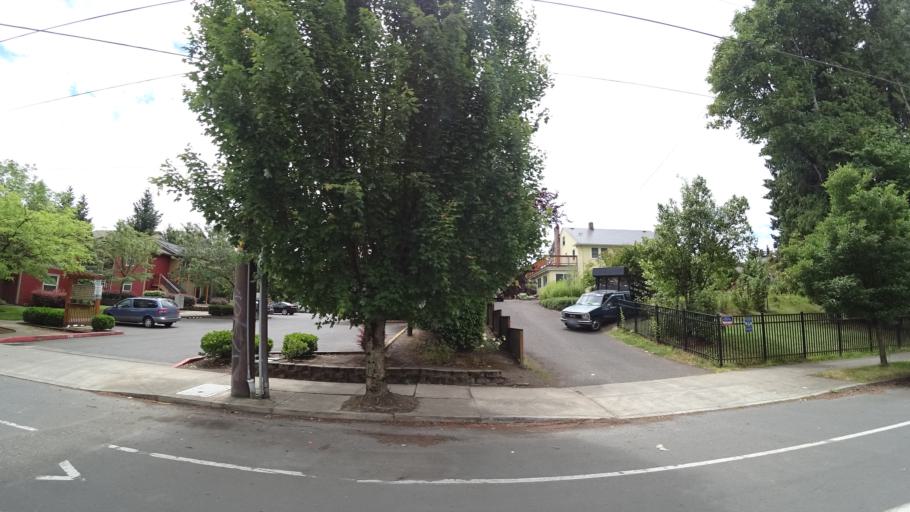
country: US
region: Oregon
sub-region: Multnomah County
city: Lents
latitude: 45.5627
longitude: -122.5965
